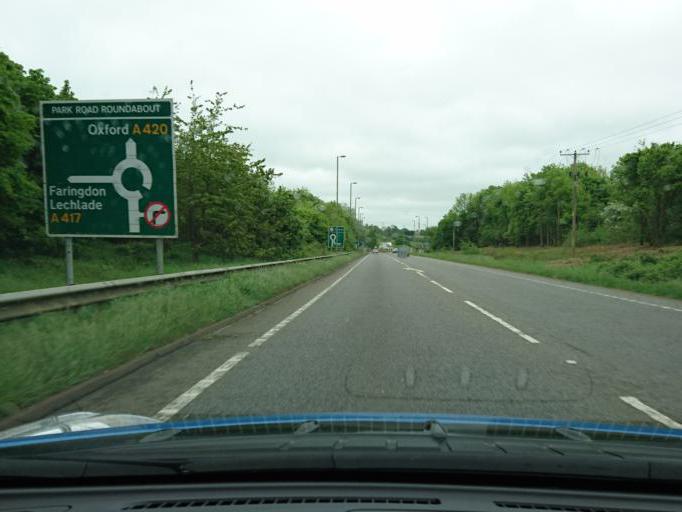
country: GB
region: England
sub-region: Oxfordshire
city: Faringdon
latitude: 51.6479
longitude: -1.5775
